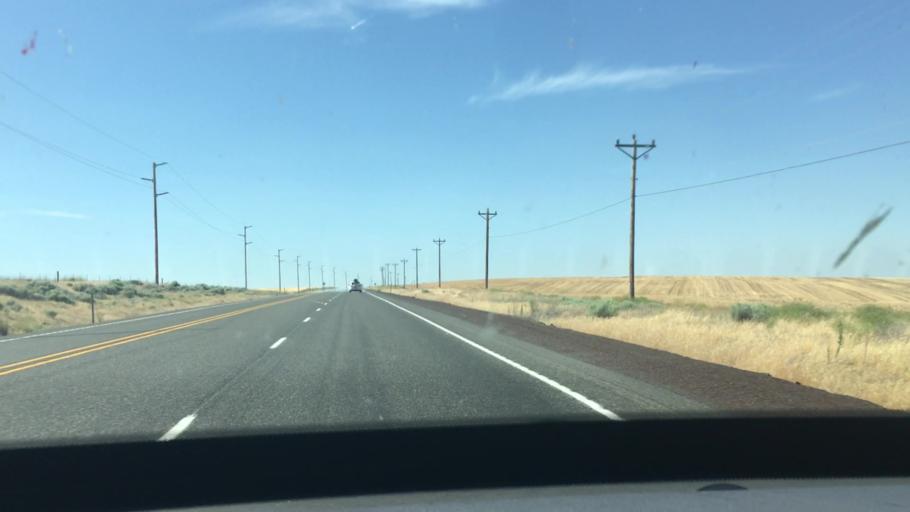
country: US
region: Oregon
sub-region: Sherman County
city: Moro
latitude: 45.5250
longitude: -120.6890
